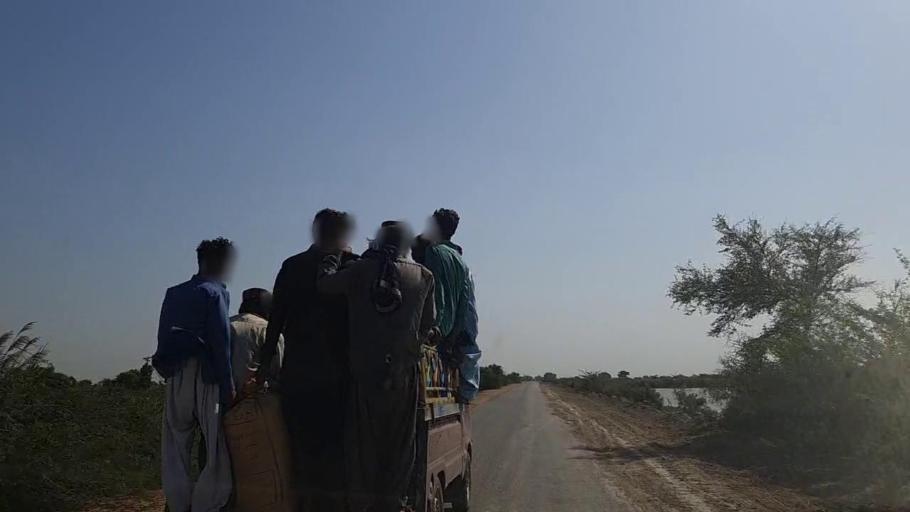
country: PK
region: Sindh
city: Mirpur Batoro
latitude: 24.6483
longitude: 68.2890
